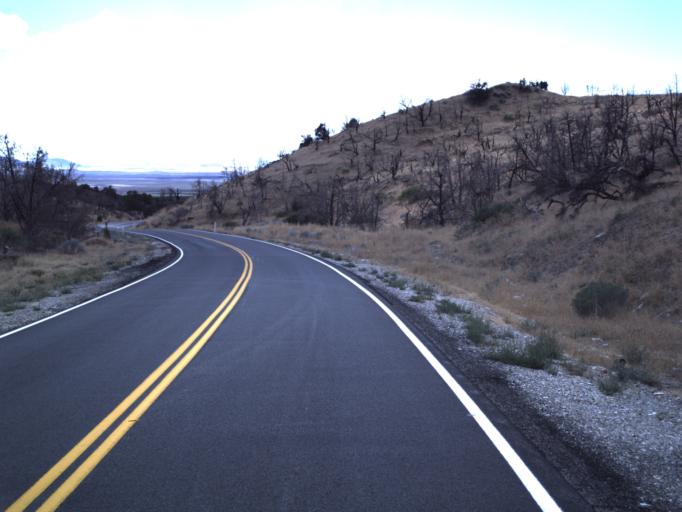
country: US
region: Utah
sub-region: Tooele County
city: Grantsville
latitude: 40.3337
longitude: -112.6163
